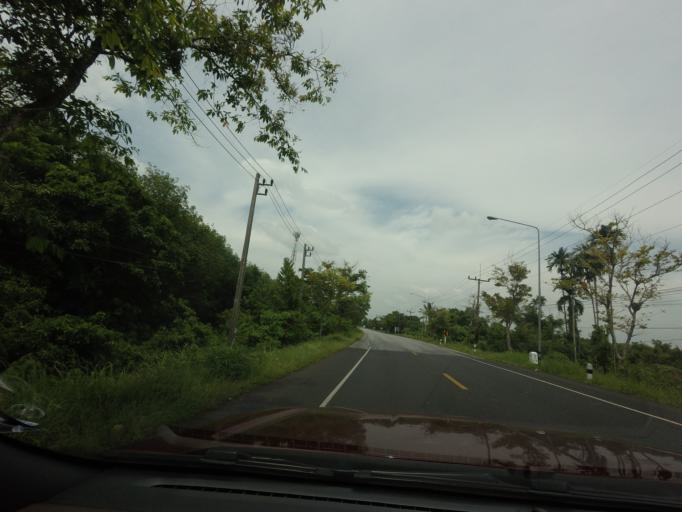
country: TH
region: Pattani
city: Mae Lan
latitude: 6.6373
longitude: 101.3022
